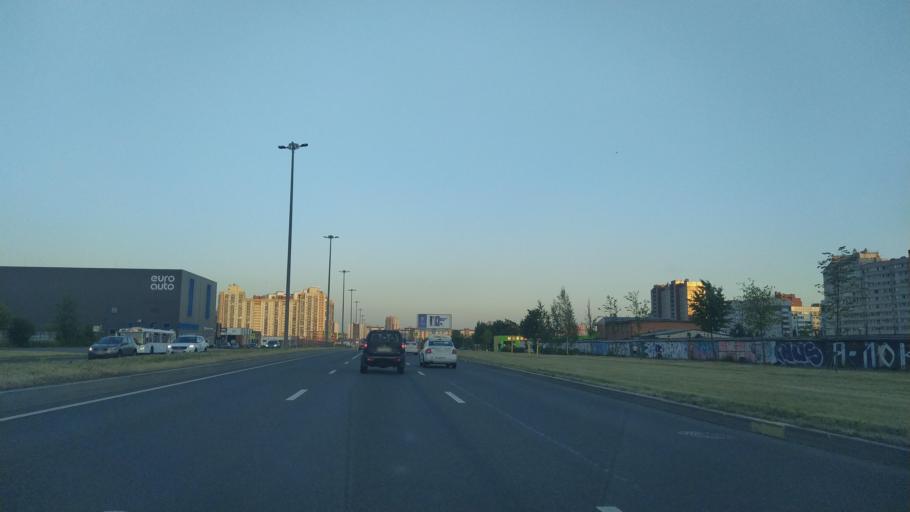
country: RU
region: St.-Petersburg
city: Kolomyagi
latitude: 60.0266
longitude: 30.2576
